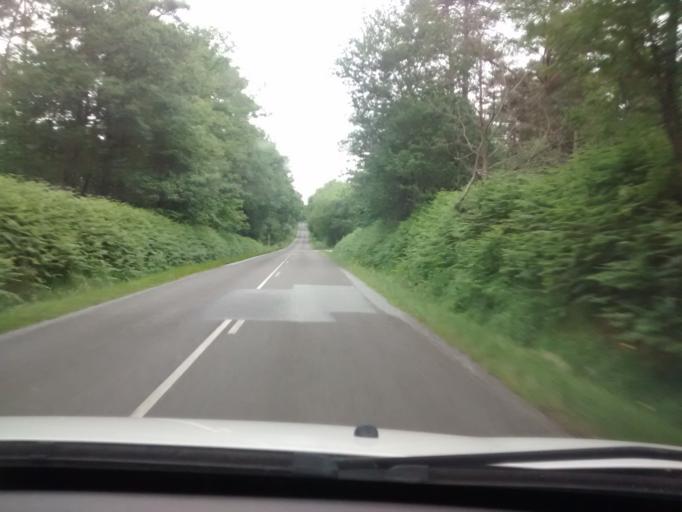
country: FR
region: Brittany
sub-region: Departement d'Ille-et-Vilaine
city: La Bouexiere
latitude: 48.1547
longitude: -1.4431
